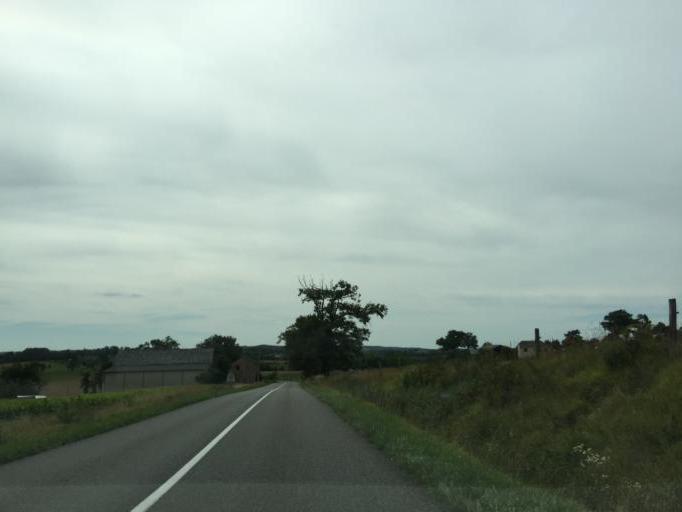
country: FR
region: Midi-Pyrenees
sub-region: Departement de l'Aveyron
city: La Fouillade
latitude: 44.2667
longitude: 2.0435
